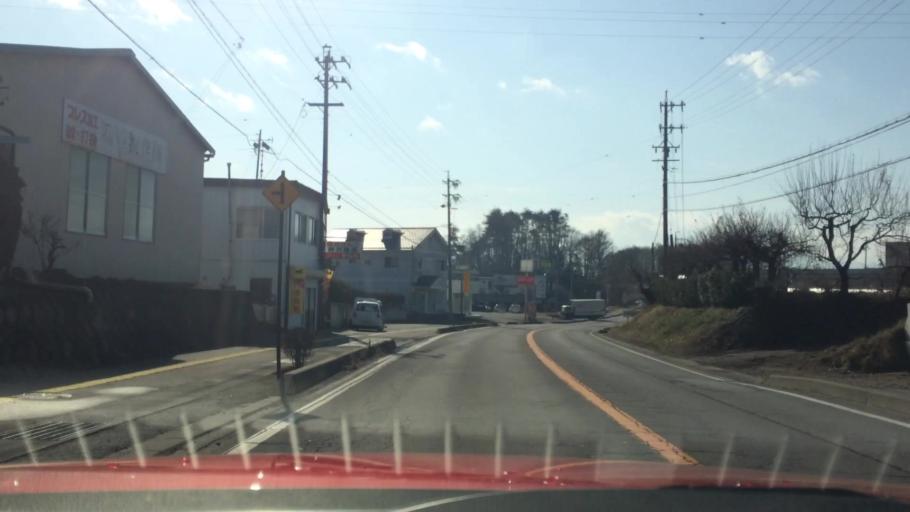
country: JP
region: Nagano
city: Komoro
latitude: 36.2920
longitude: 138.4910
